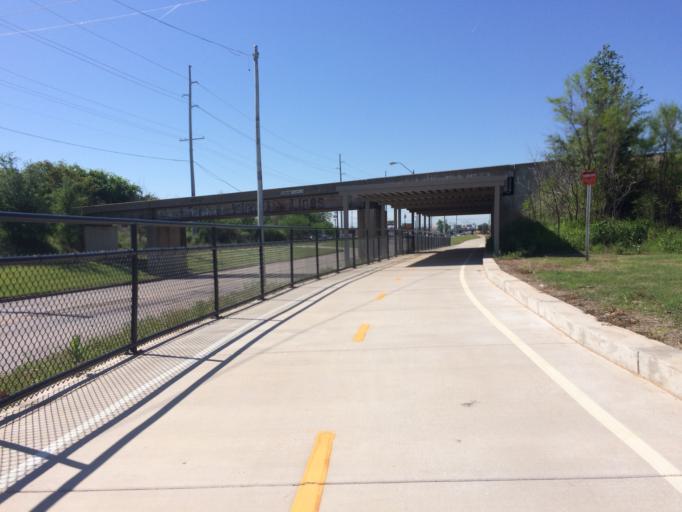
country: US
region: Oklahoma
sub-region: Oklahoma County
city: Oklahoma City
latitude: 35.4677
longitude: -97.5658
